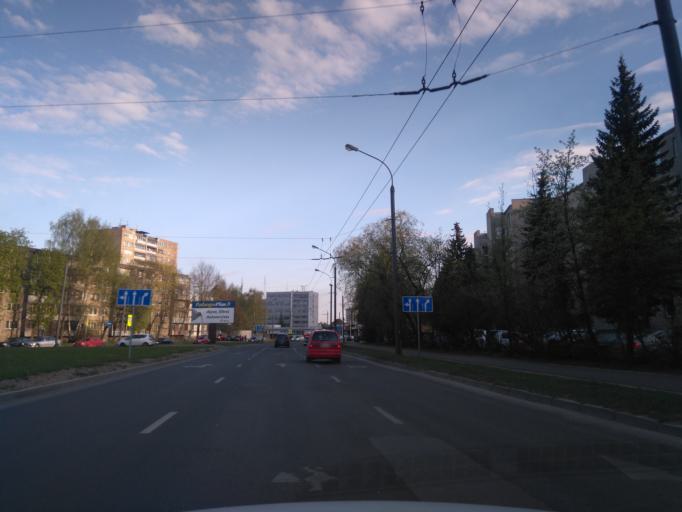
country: LT
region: Kauno apskritis
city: Dainava (Kaunas)
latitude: 54.9149
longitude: 23.9557
